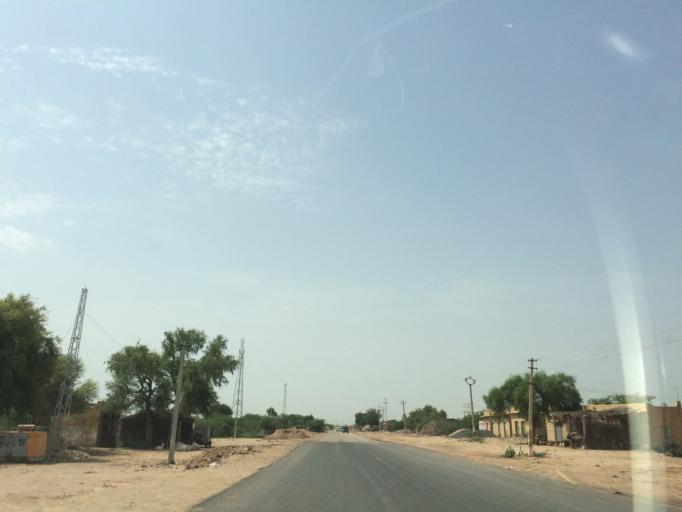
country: IN
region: Rajasthan
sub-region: Jaisalmer
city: Jaisalmer
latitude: 26.6964
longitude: 71.1986
